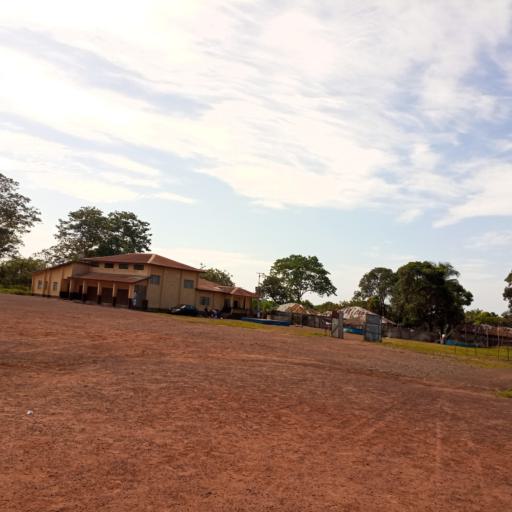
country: SL
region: Northern Province
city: Kambia
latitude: 9.1235
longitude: -12.9148
